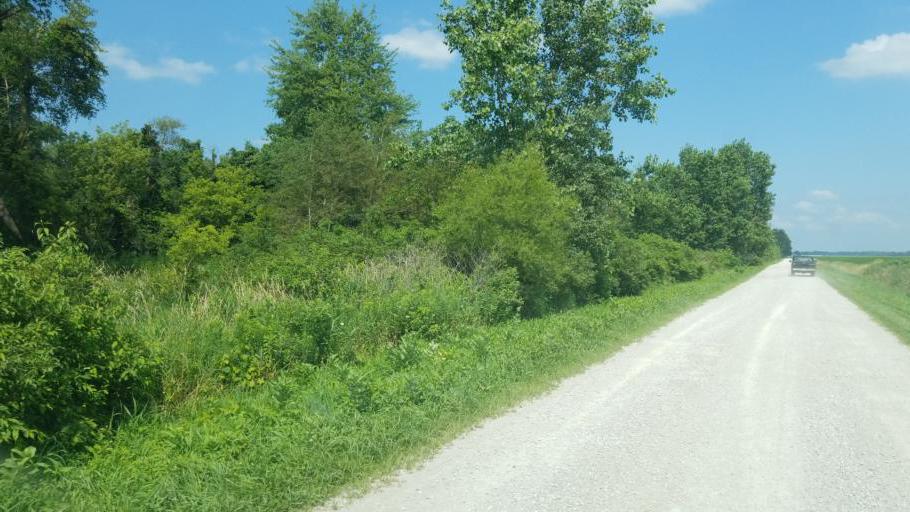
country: US
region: Ohio
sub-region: Huron County
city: Willard
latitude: 40.9959
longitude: -82.7708
